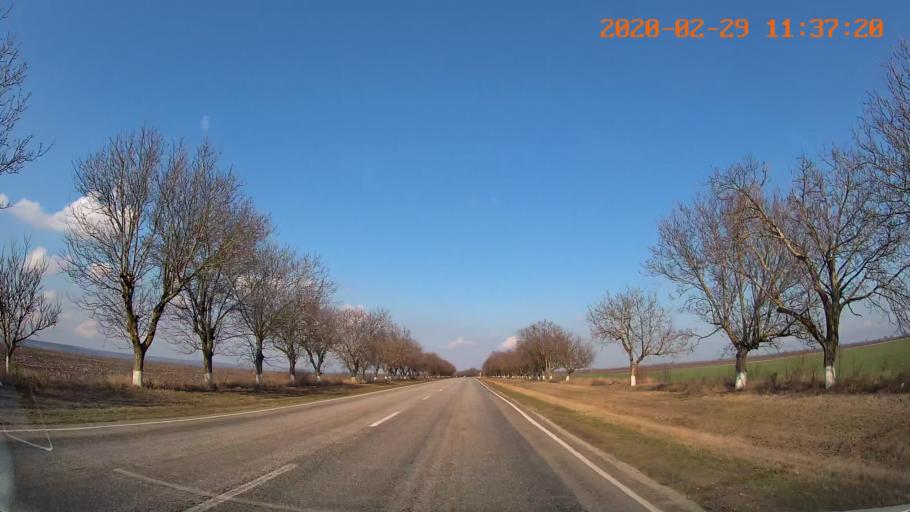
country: MD
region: Rezina
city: Saharna
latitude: 47.6101
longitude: 29.0470
